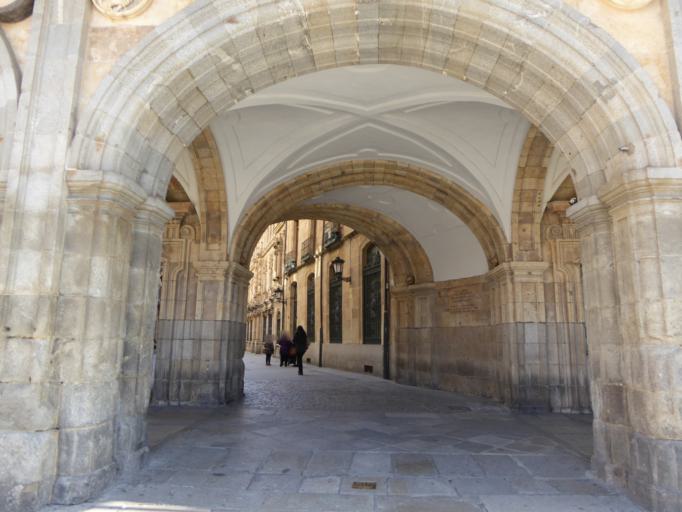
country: ES
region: Castille and Leon
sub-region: Provincia de Salamanca
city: Salamanca
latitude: 40.9654
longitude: -5.6640
